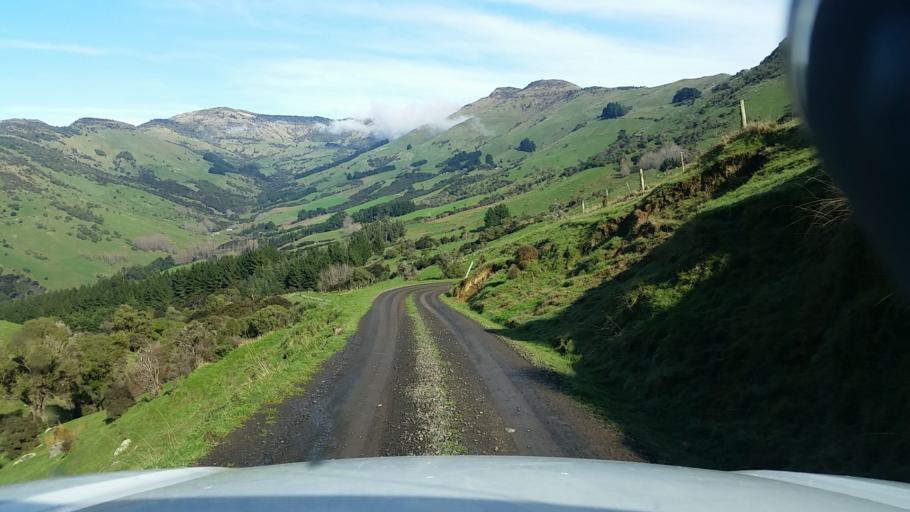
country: NZ
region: Canterbury
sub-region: Christchurch City
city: Christchurch
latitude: -43.6650
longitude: 172.8718
